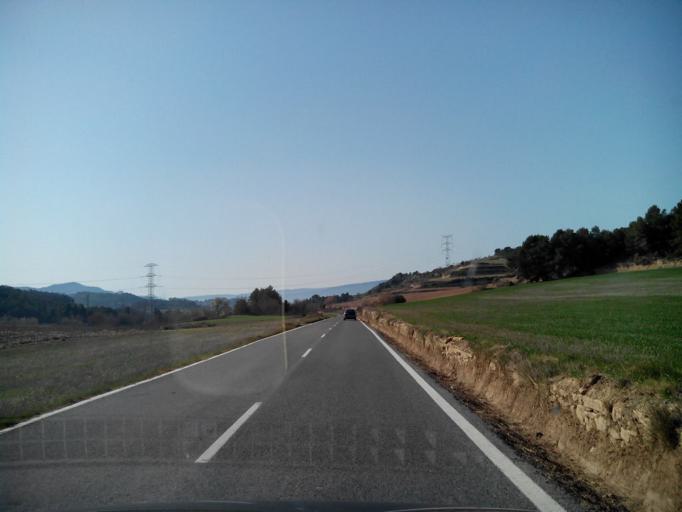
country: ES
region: Catalonia
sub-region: Provincia de Tarragona
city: Fores
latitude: 41.4679
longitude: 1.2727
